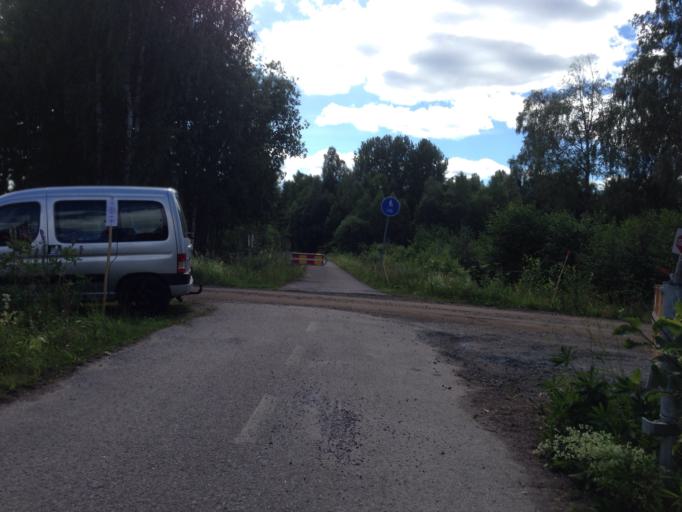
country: SE
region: Dalarna
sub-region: Ludvika Kommun
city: Ludvika
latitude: 60.2055
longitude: 15.1049
